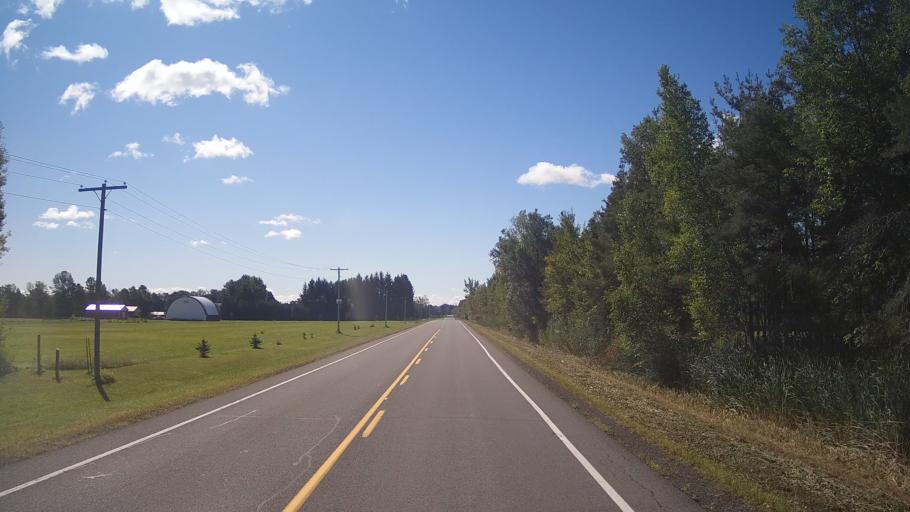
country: CA
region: Ontario
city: Prescott
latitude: 44.9147
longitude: -75.4095
